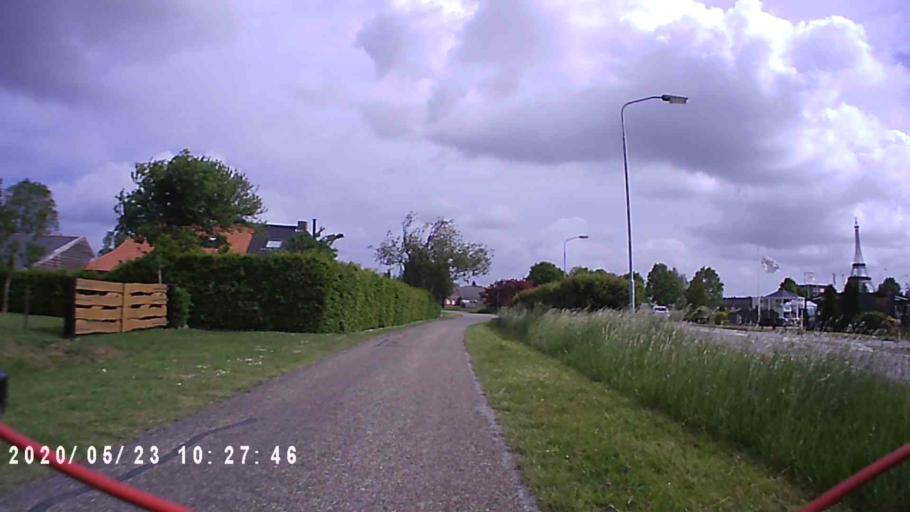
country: NL
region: Groningen
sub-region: Gemeente Appingedam
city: Appingedam
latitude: 53.3006
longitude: 6.8516
